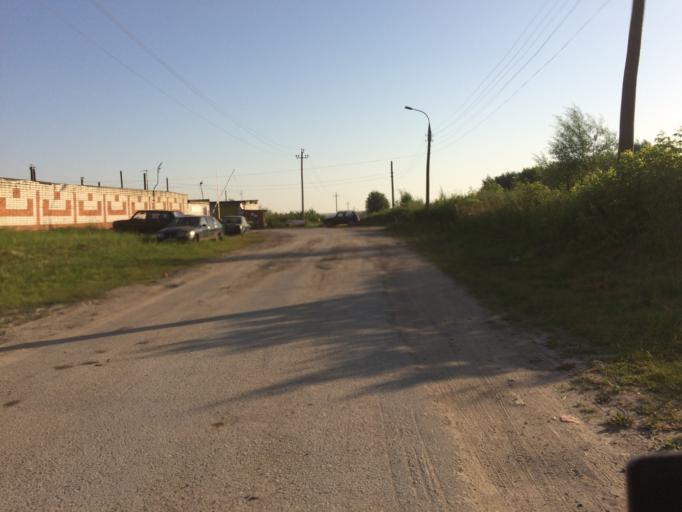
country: RU
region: Mariy-El
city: Yoshkar-Ola
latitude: 56.6563
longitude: 47.8880
